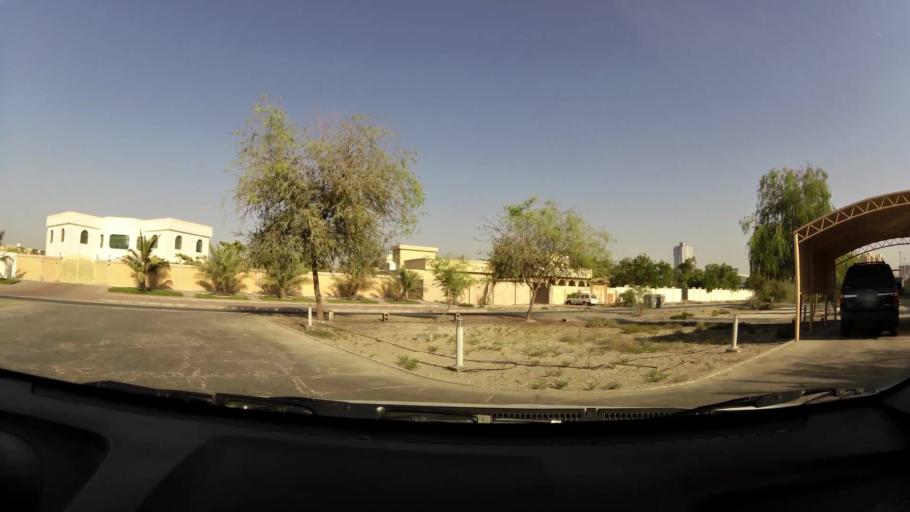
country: AE
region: Ajman
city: Ajman
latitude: 25.4020
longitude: 55.4577
